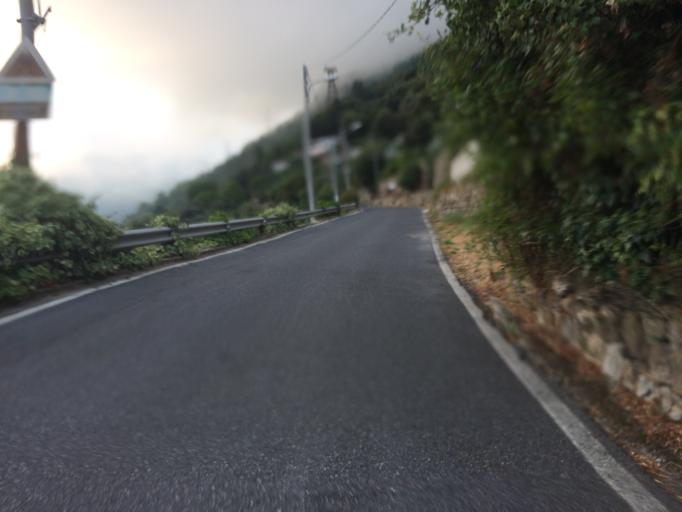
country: IT
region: Liguria
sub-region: Provincia di Imperia
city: San Remo
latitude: 43.8438
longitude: 7.7414
